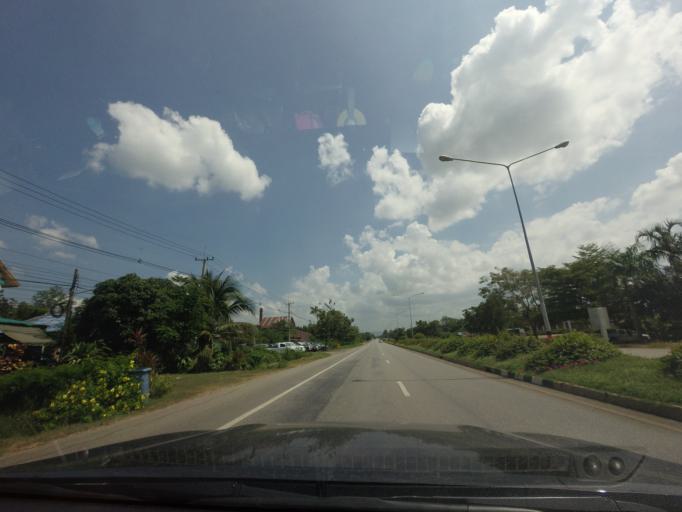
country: TH
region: Phetchabun
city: Phetchabun
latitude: 16.2586
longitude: 101.0564
